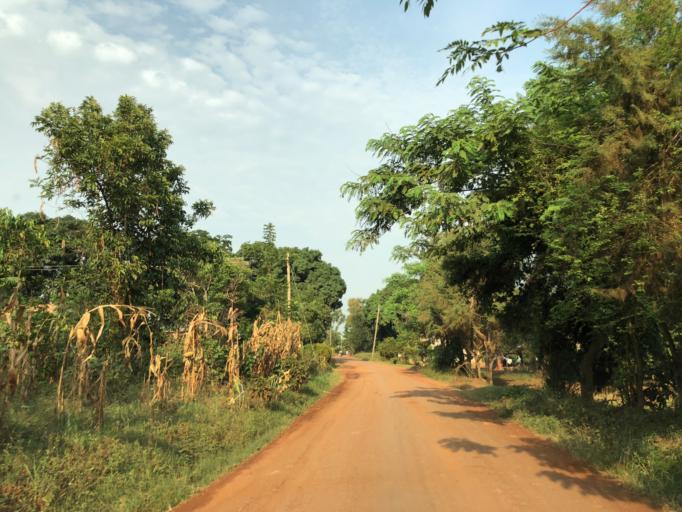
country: UG
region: Central Region
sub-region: Wakiso District
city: Bweyogerere
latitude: 0.4738
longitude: 32.6393
